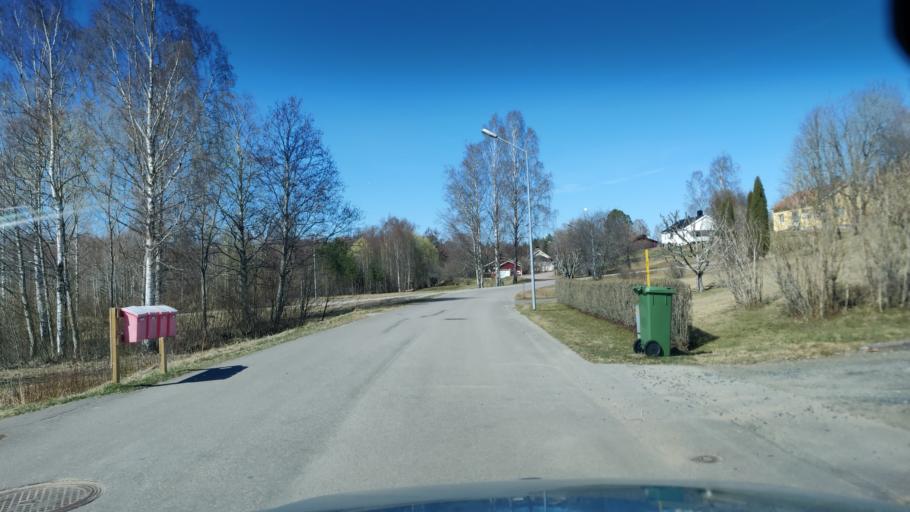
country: SE
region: Vaermland
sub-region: Hagfors Kommun
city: Hagfors
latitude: 60.0380
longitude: 13.6828
